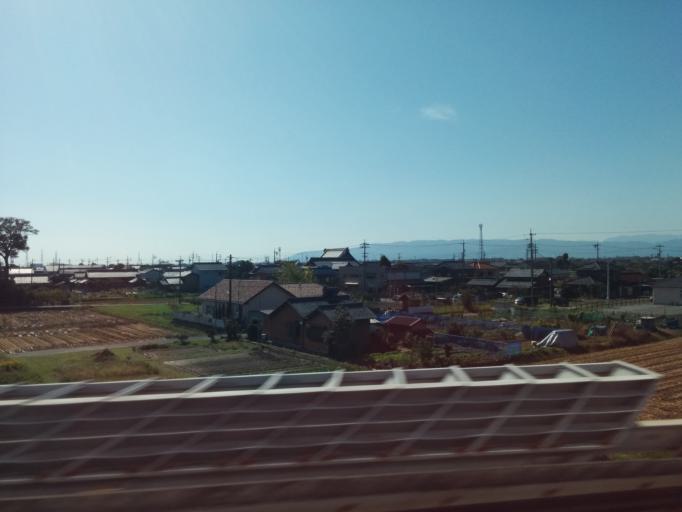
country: JP
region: Aichi
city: Sobue
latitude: 35.2908
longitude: 136.7349
